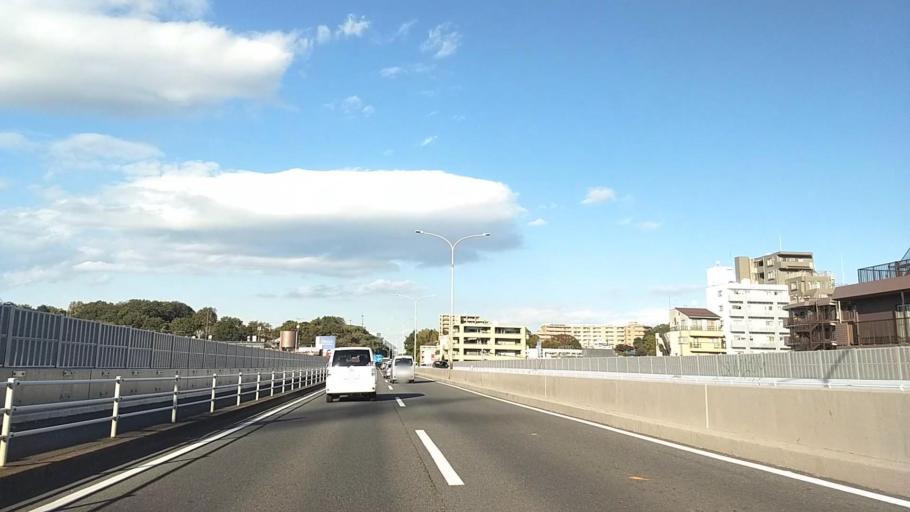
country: JP
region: Tokyo
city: Chofugaoka
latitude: 35.5998
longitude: 139.6050
